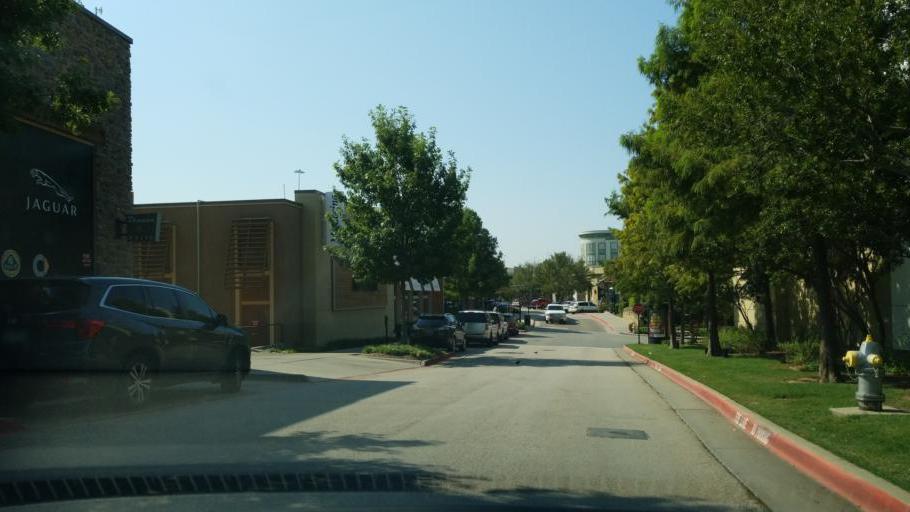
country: US
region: Texas
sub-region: Collin County
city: Allen
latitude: 33.0900
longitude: -96.6835
